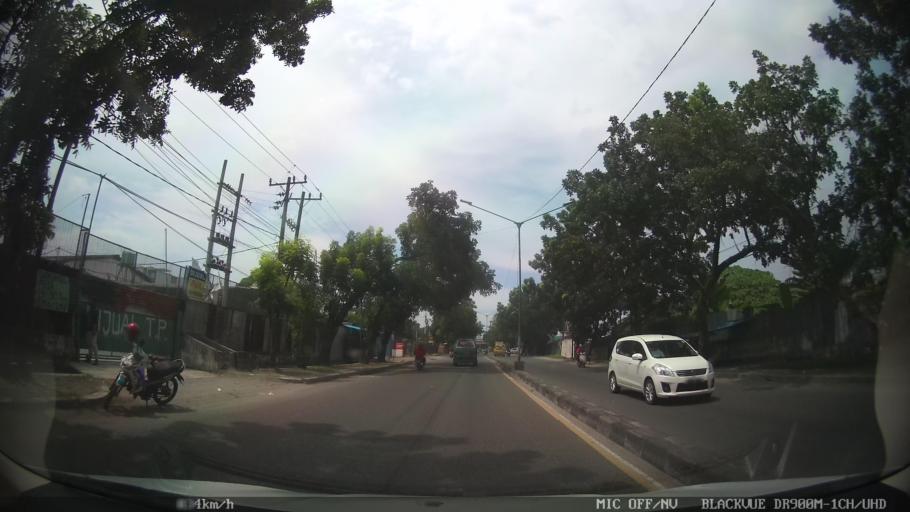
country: ID
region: North Sumatra
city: Medan
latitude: 3.6452
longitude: 98.6628
